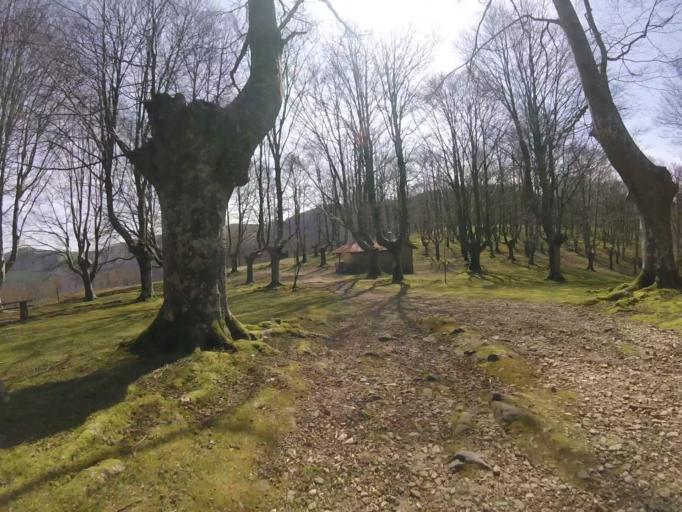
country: ES
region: Navarre
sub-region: Provincia de Navarra
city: Arano
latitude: 43.2530
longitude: -1.8256
